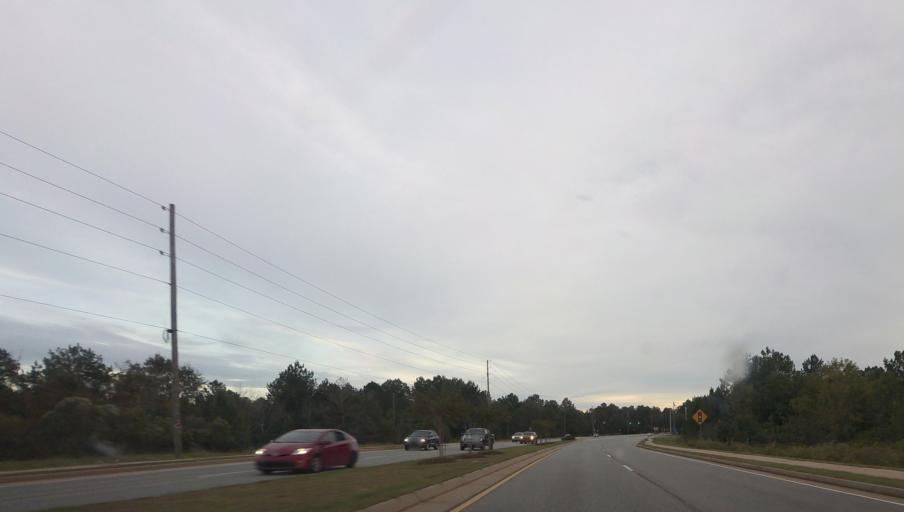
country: US
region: Georgia
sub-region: Houston County
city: Centerville
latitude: 32.5502
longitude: -83.6610
